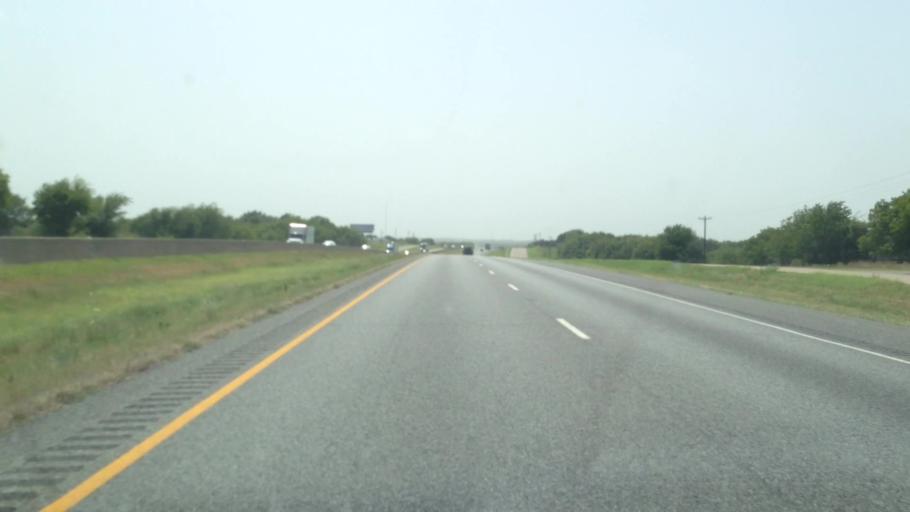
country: US
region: Texas
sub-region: Hunt County
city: Commerce
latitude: 33.1302
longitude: -95.8906
